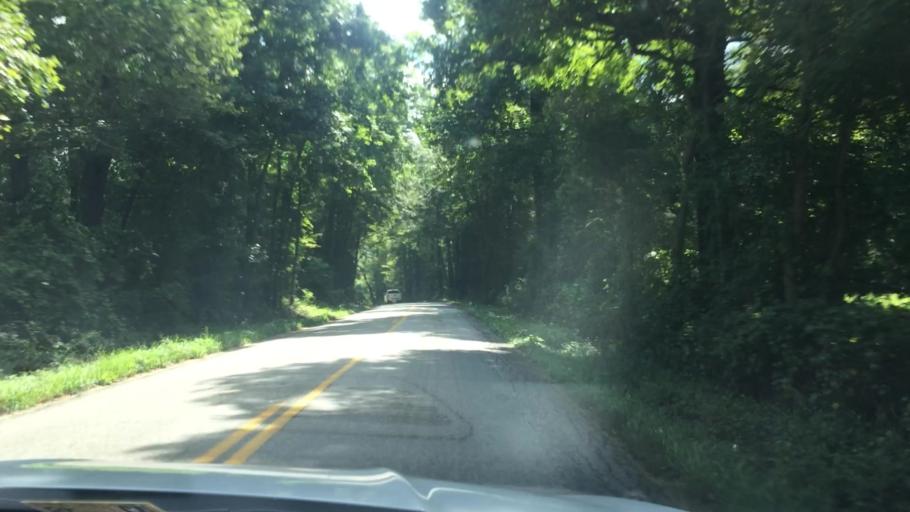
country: US
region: Virginia
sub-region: Charles City County
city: Charles City
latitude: 37.4112
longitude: -77.0365
